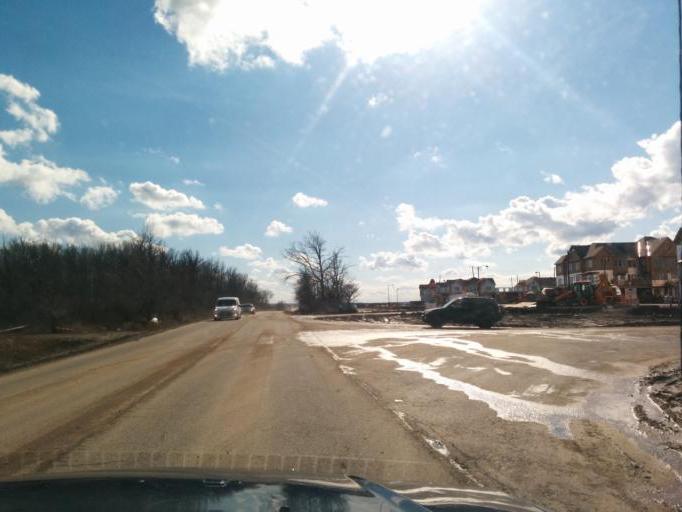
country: CA
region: Ontario
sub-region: Halton
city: Milton
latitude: 43.4841
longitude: -79.8376
